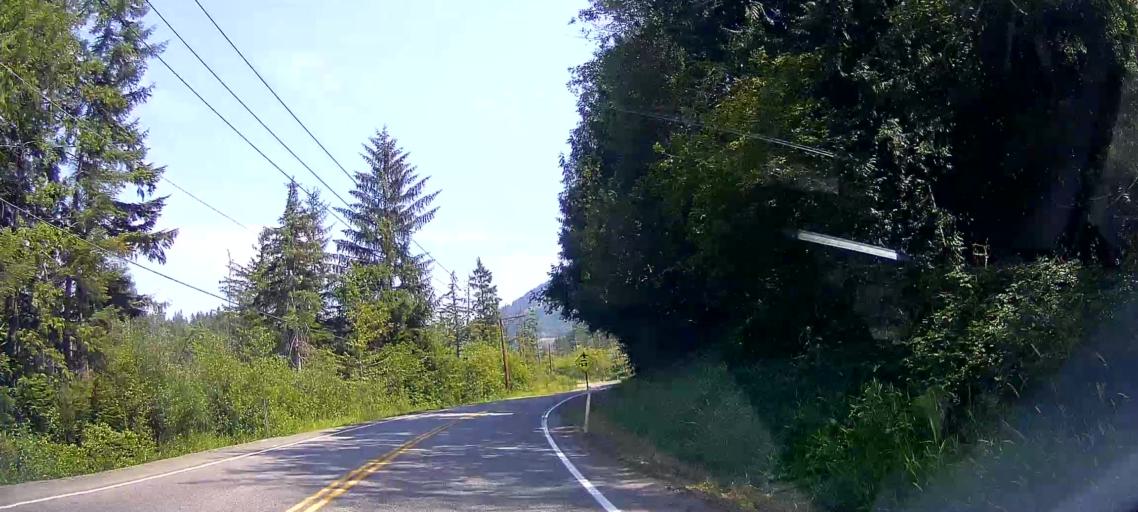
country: US
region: Washington
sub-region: Snohomish County
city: Bryant
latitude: 48.3274
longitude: -122.1546
